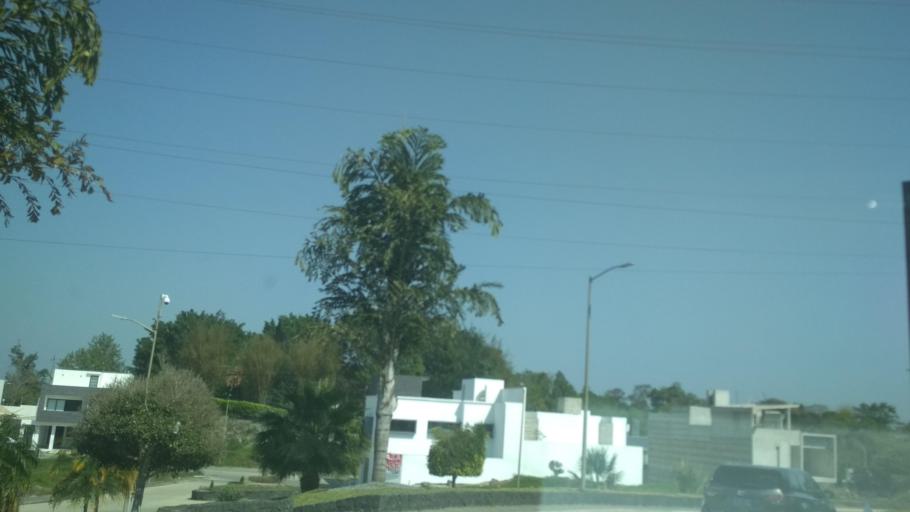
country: MX
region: Veracruz
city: El Castillo
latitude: 19.5278
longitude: -96.8641
